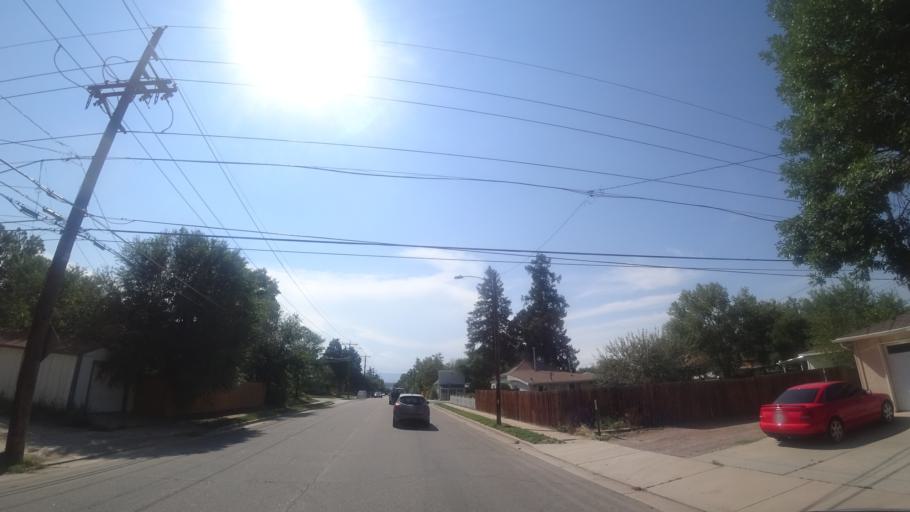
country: US
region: Colorado
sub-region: Arapahoe County
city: Englewood
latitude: 39.6386
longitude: -104.9906
